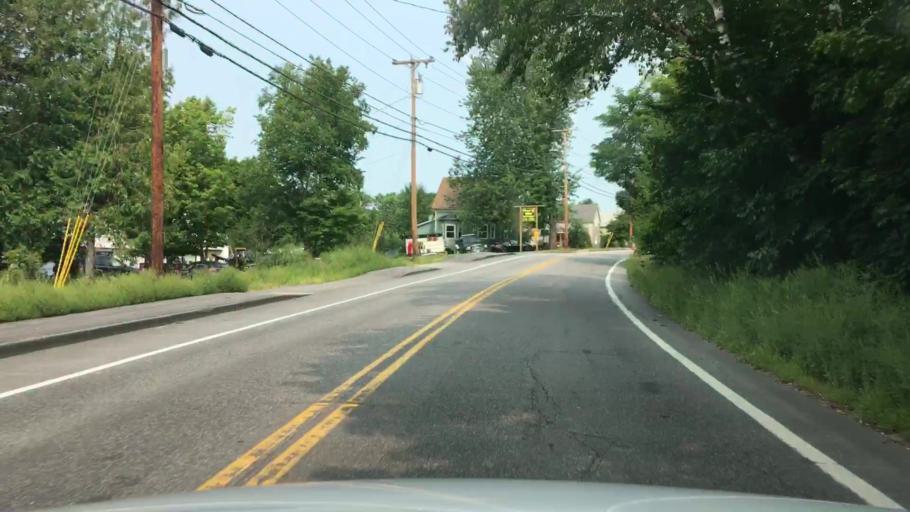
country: US
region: Maine
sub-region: Androscoggin County
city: Livermore Falls
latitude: 44.4654
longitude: -70.1819
